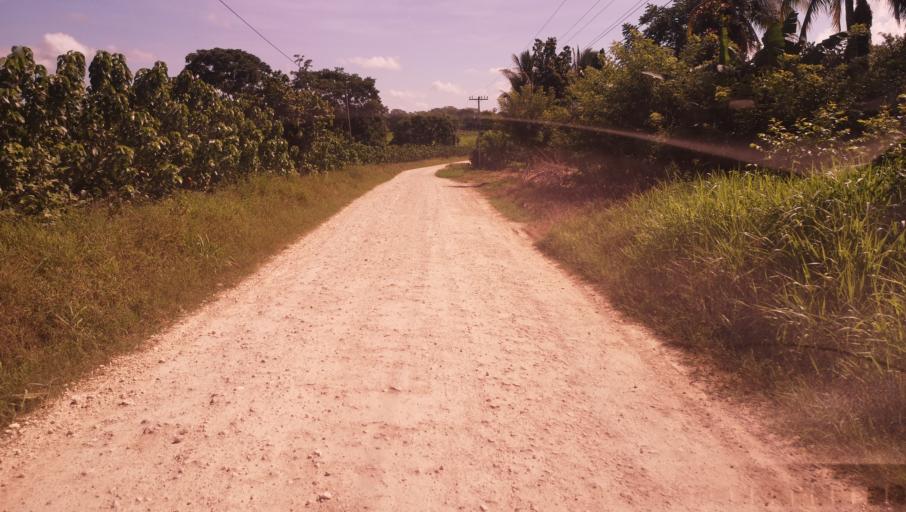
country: GT
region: Peten
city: Dolores
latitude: 16.7880
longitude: -89.3070
